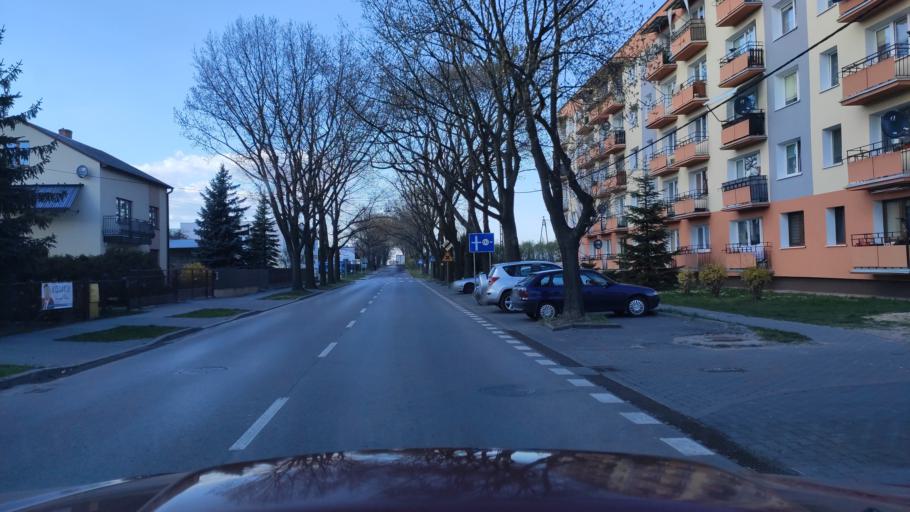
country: PL
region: Masovian Voivodeship
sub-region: Powiat zwolenski
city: Zwolen
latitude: 51.3597
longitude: 21.5758
